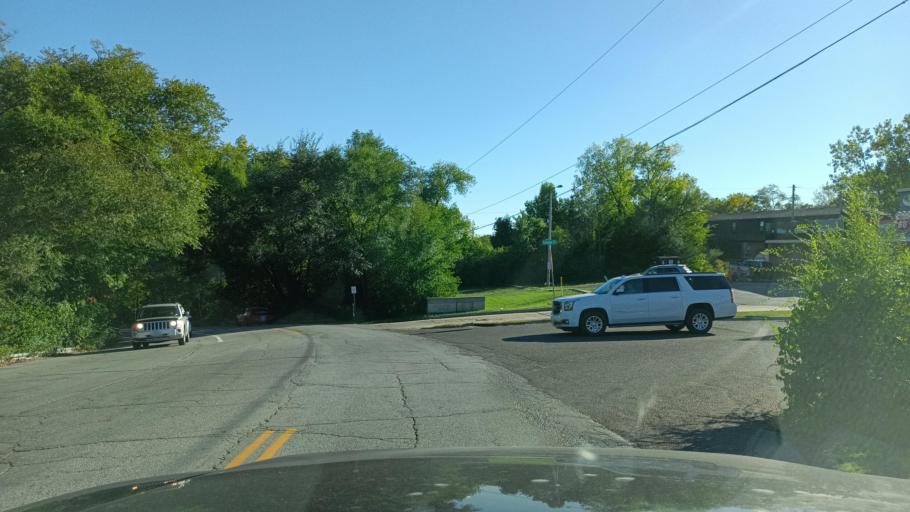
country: US
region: Missouri
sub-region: Boone County
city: Columbia
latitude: 38.9341
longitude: -92.3235
